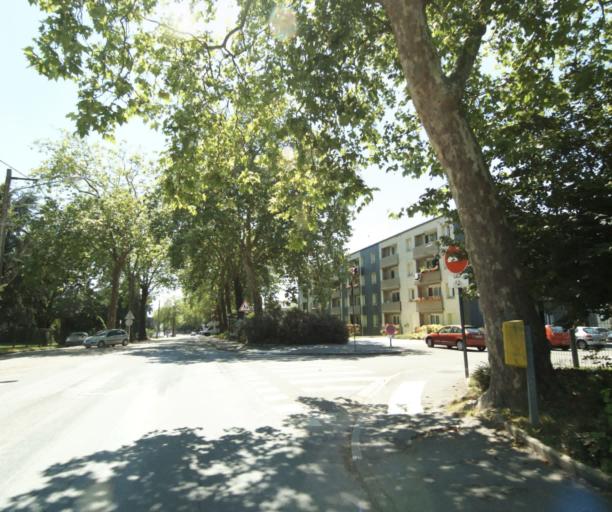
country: FR
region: Pays de la Loire
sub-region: Departement de la Mayenne
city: Laval
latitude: 48.0843
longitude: -0.7550
